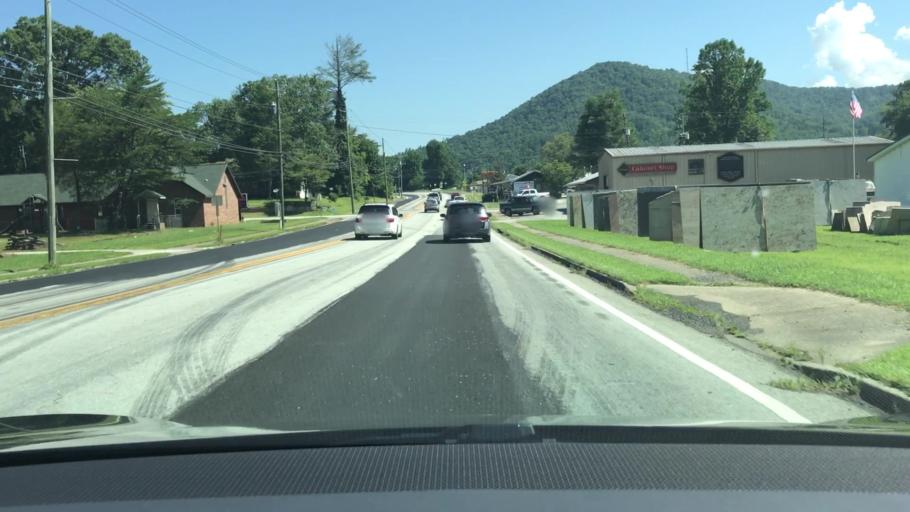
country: US
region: Georgia
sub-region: Rabun County
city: Mountain City
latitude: 34.9163
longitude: -83.3861
